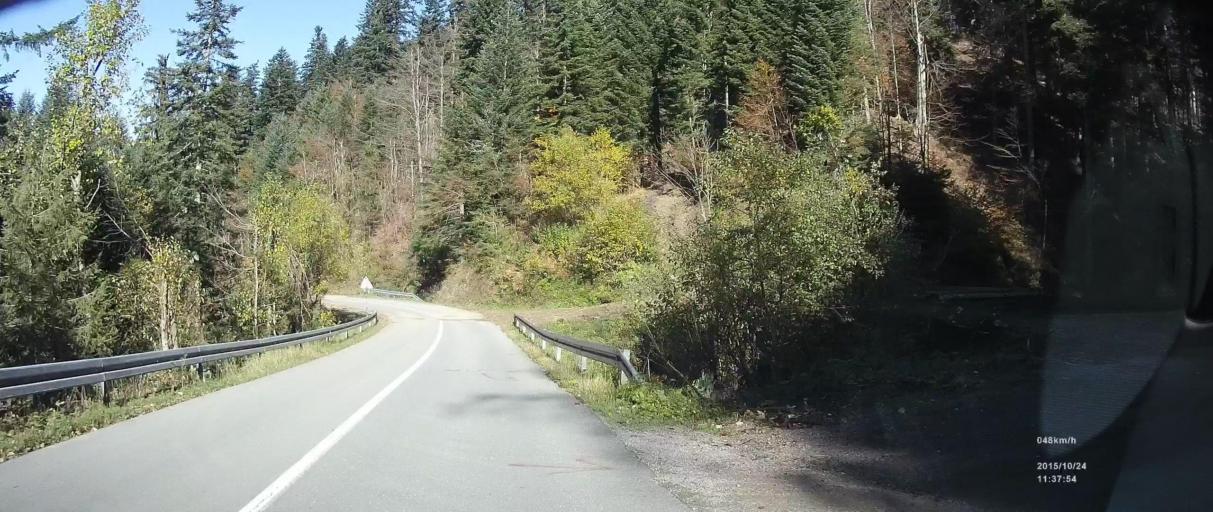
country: HR
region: Primorsko-Goranska
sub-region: Grad Delnice
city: Delnice
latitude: 45.4009
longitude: 14.7028
